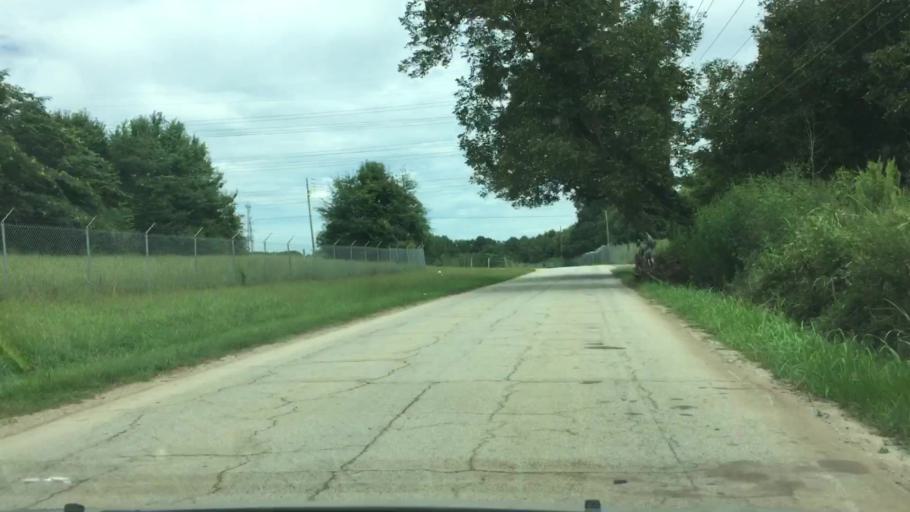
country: US
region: Georgia
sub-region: DeKalb County
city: Gresham Park
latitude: 33.6974
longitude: -84.3380
